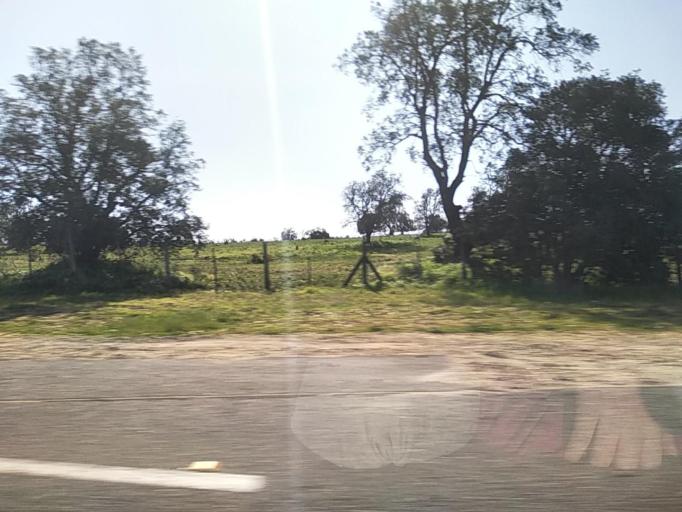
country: CL
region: Valparaiso
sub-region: San Antonio Province
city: El Tabo
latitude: -33.4070
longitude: -71.5463
